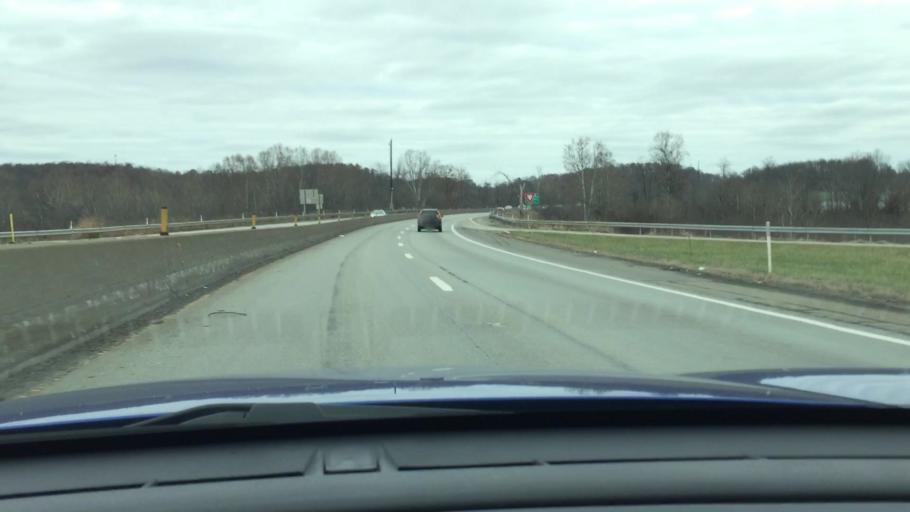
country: US
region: Pennsylvania
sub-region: Westmoreland County
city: New Stanton
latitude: 40.2093
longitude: -79.6766
